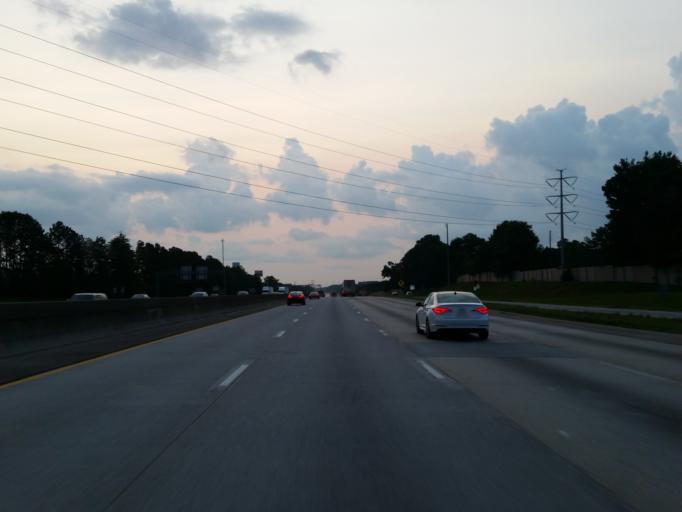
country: US
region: Georgia
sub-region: Clayton County
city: Morrow
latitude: 33.5654
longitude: -84.3207
